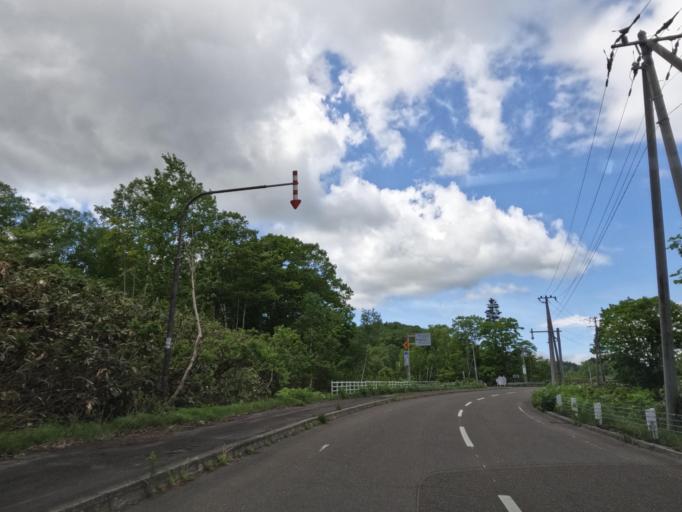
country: JP
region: Hokkaido
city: Tobetsu
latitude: 43.4734
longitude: 141.5949
